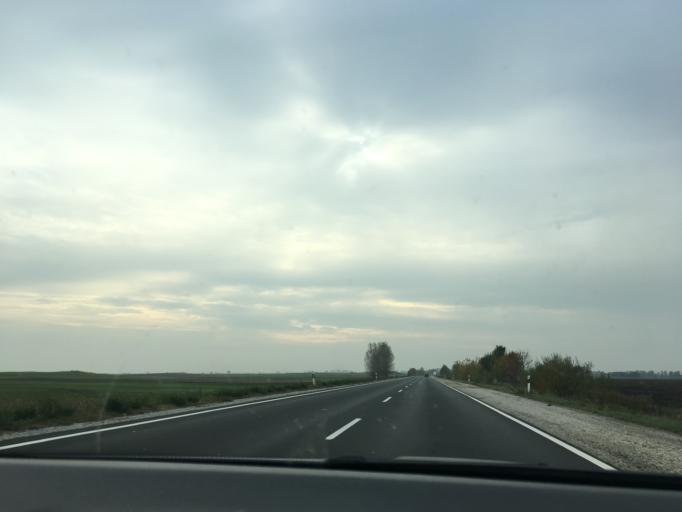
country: HU
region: Pest
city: Abony
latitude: 47.2068
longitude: 19.9612
